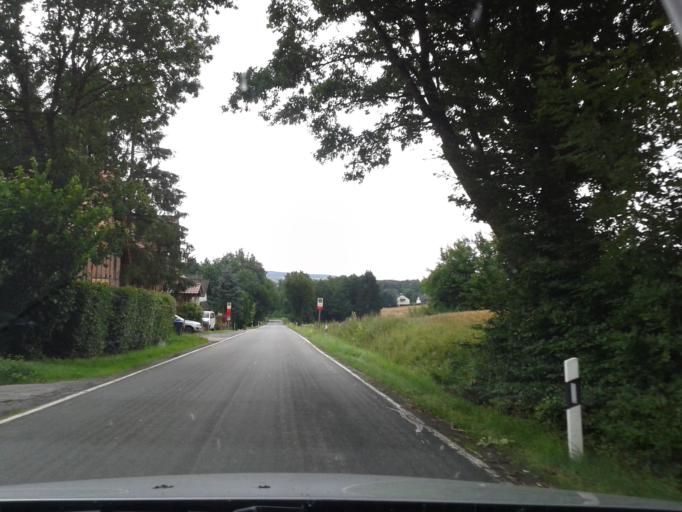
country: DE
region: North Rhine-Westphalia
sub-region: Regierungsbezirk Detmold
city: Blomberg
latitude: 51.9429
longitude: 9.1436
